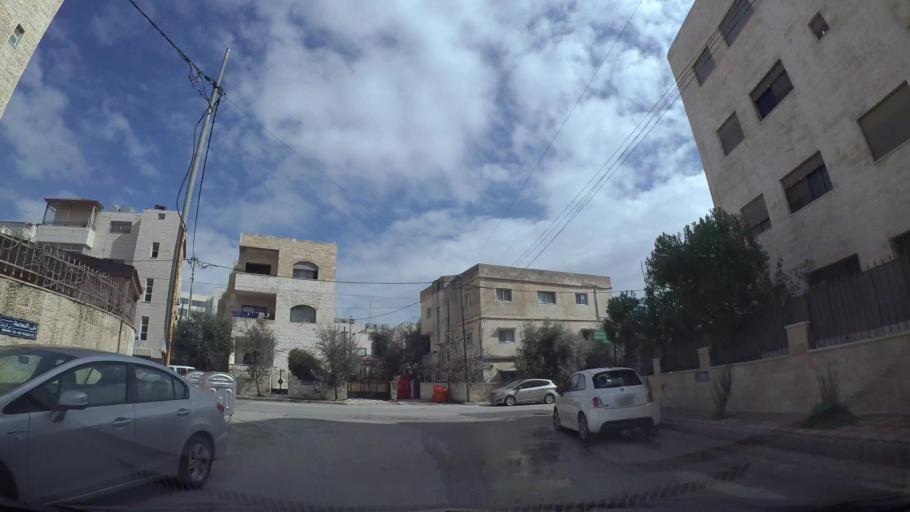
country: JO
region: Amman
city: Wadi as Sir
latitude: 31.9525
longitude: 35.8351
